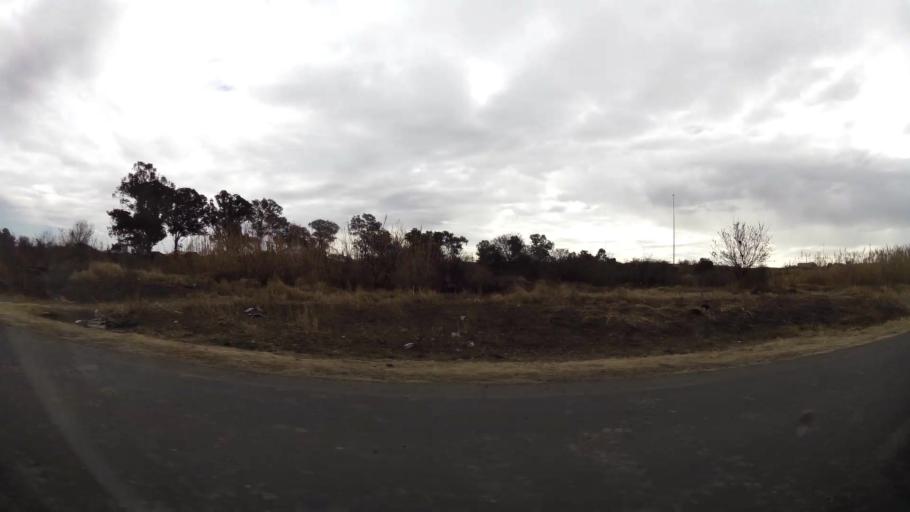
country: ZA
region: Orange Free State
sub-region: Fezile Dabi District Municipality
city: Kroonstad
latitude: -27.6515
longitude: 27.2268
